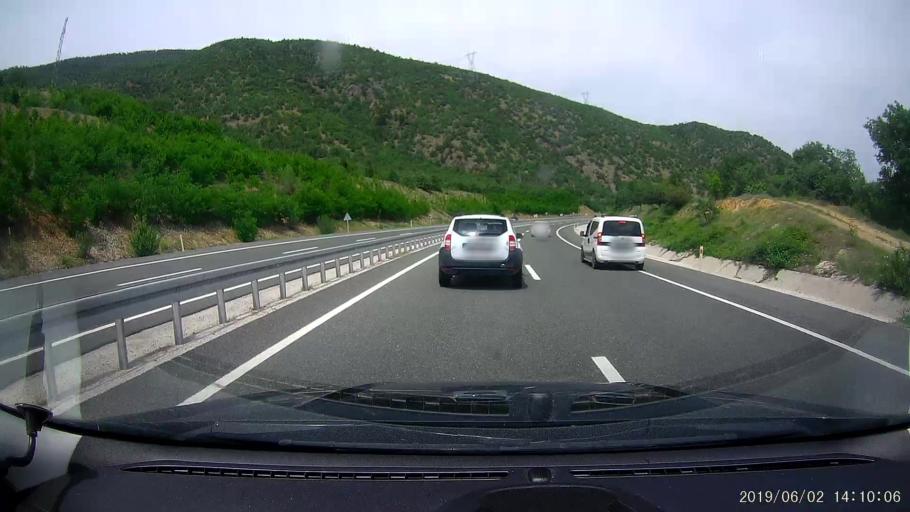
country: TR
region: Cankiri
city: Ilgaz
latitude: 40.9016
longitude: 33.7530
